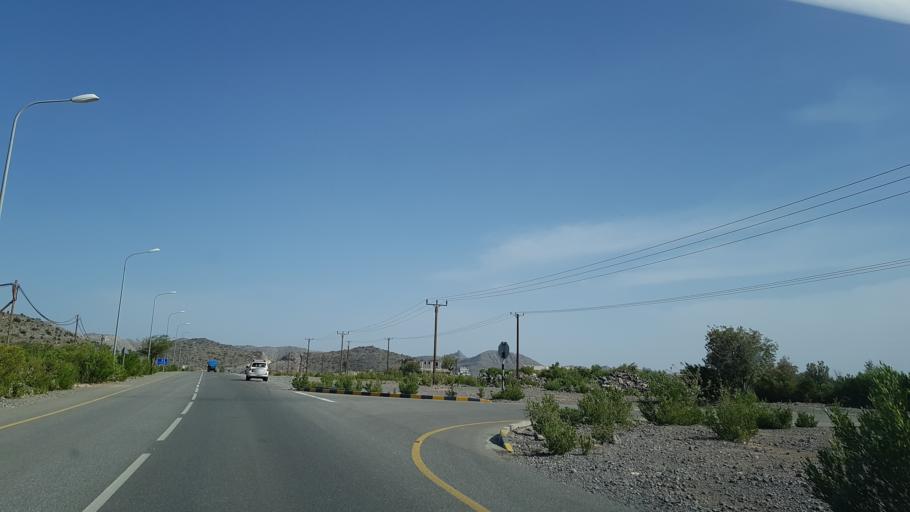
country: OM
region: Muhafazat ad Dakhiliyah
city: Izki
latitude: 23.0877
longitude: 57.6941
